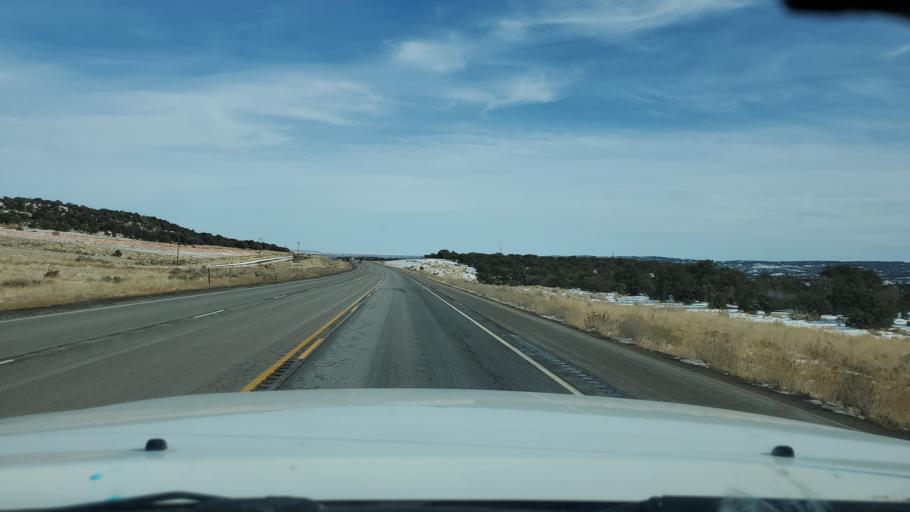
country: US
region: Utah
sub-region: Duchesne County
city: Duchesne
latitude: 40.1715
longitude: -110.5746
